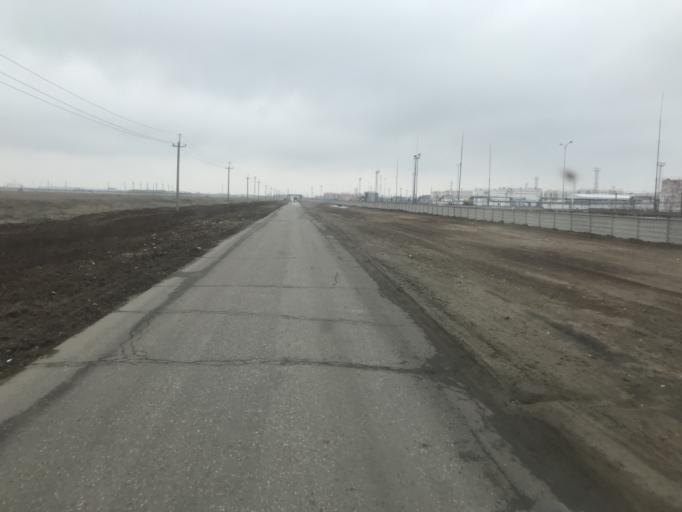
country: RU
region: Volgograd
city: Svetlyy Yar
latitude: 48.5044
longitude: 44.6459
